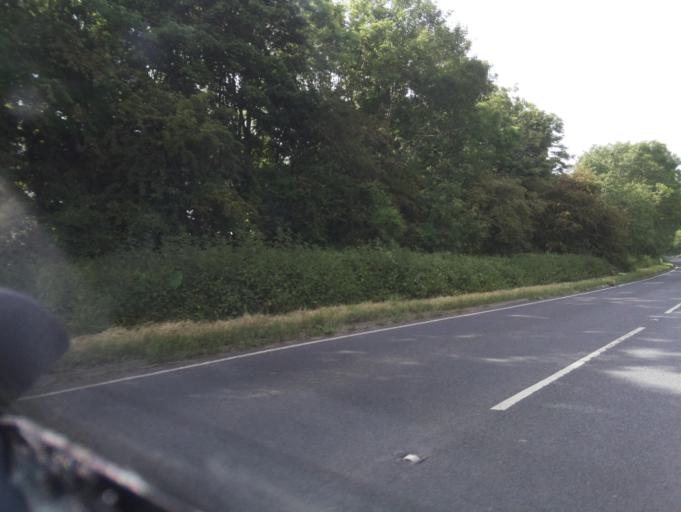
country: GB
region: England
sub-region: Worcestershire
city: Pershore
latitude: 52.1259
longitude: -2.1040
